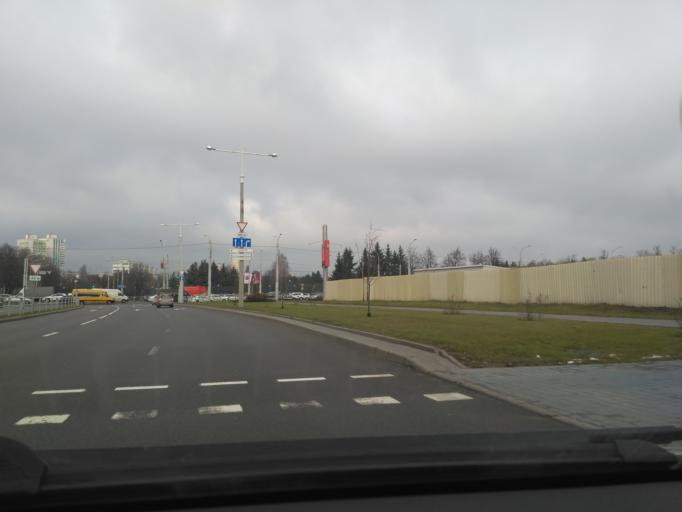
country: BY
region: Minsk
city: Borovlyany
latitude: 53.9347
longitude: 27.6566
